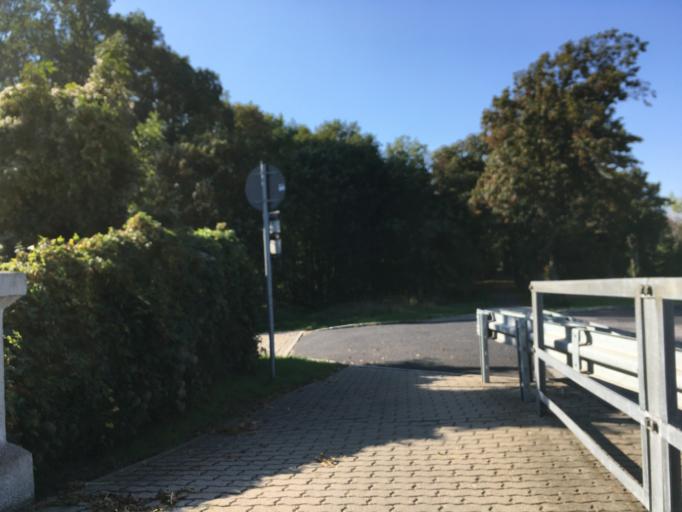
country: PL
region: Lubusz
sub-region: Powiat gorzowski
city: Kostrzyn nad Odra
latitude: 52.5783
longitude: 14.6282
